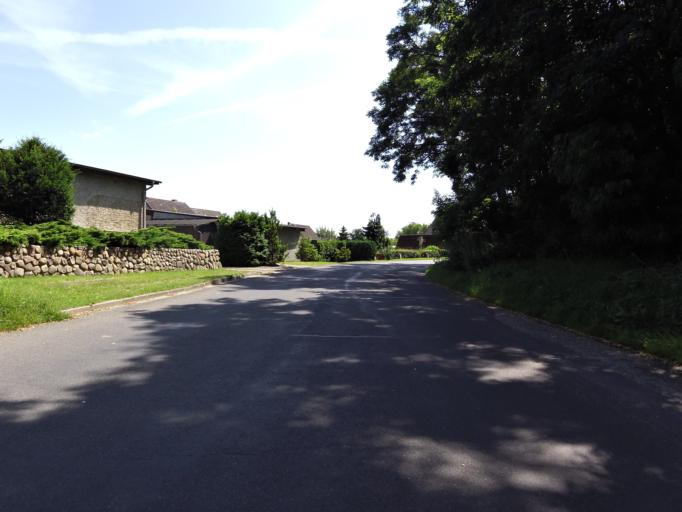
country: DE
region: Brandenburg
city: Furstenberg
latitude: 53.1906
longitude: 13.1418
